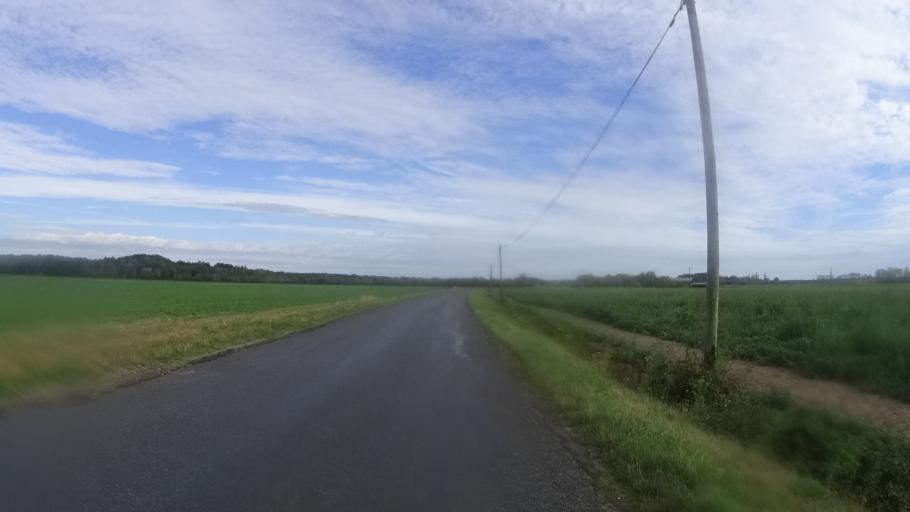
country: FR
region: Centre
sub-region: Departement du Loiret
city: Chateauneuf-sur-Loire
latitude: 47.8823
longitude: 2.2141
